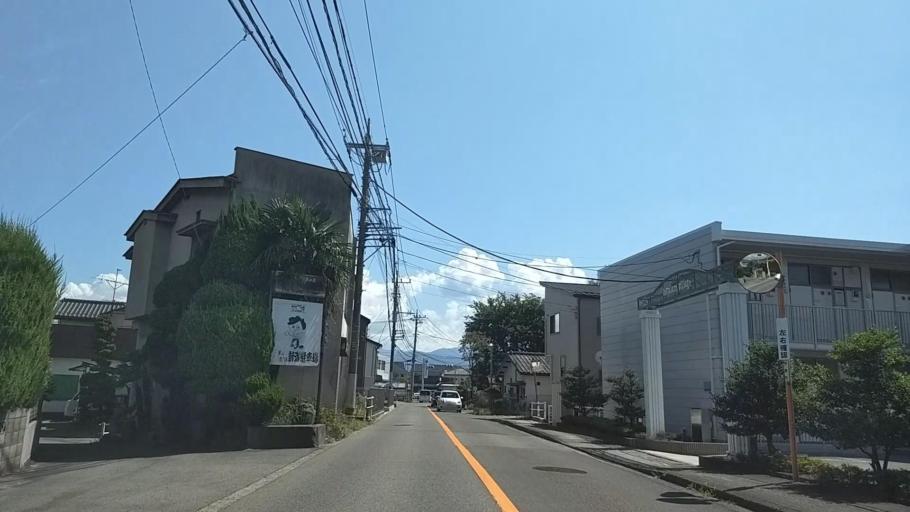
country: JP
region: Yamanashi
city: Ryuo
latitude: 35.6481
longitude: 138.5170
